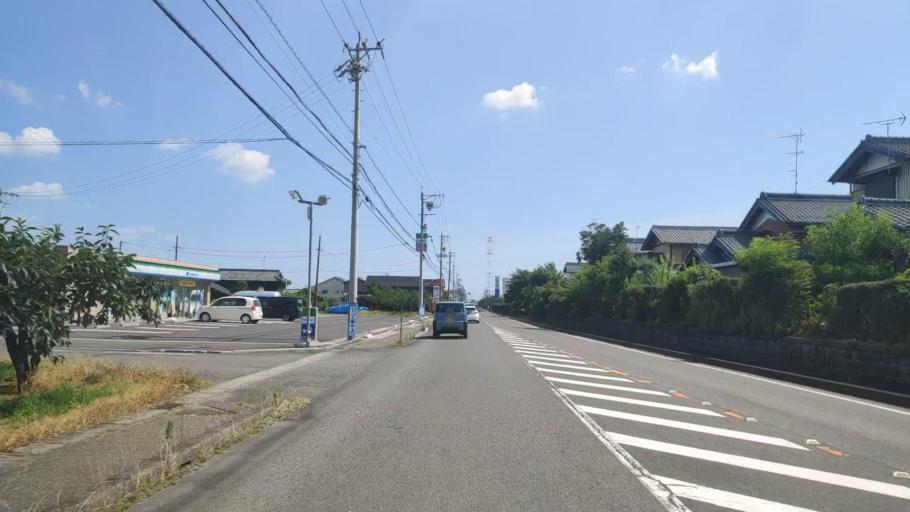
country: JP
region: Gifu
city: Godo
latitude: 35.4682
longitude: 136.6753
